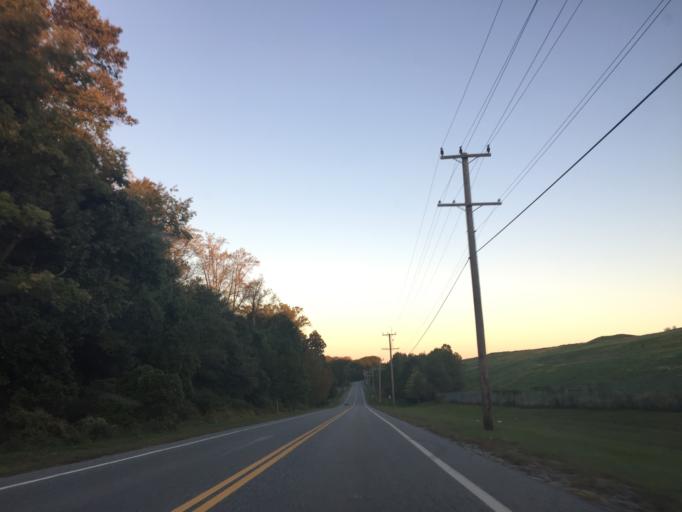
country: US
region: Maryland
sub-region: Baltimore County
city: White Marsh
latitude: 39.3984
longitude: -76.3978
